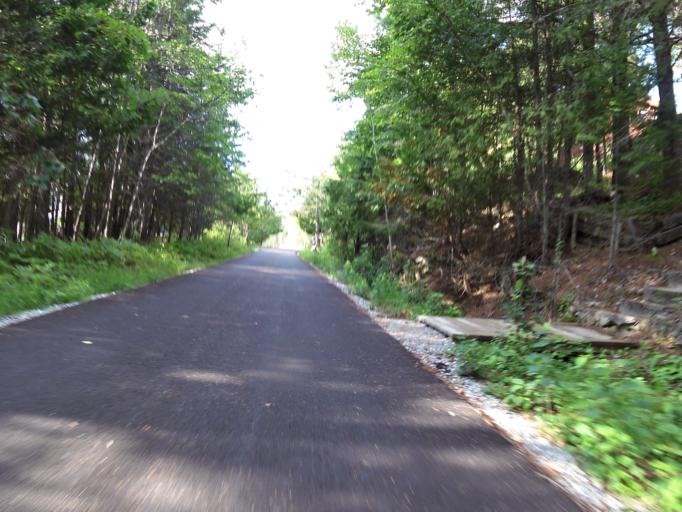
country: CA
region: Quebec
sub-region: Outaouais
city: Maniwaki
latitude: 46.2092
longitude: -76.0394
